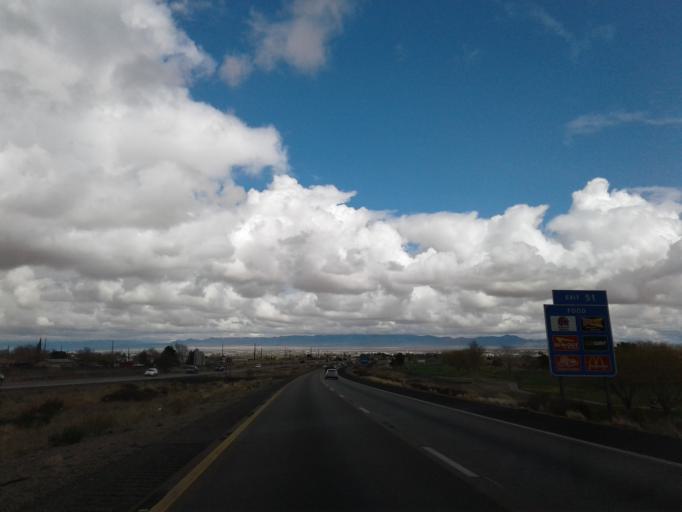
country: US
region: Arizona
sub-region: Mohave County
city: Kingman
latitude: 35.2096
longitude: -114.0559
